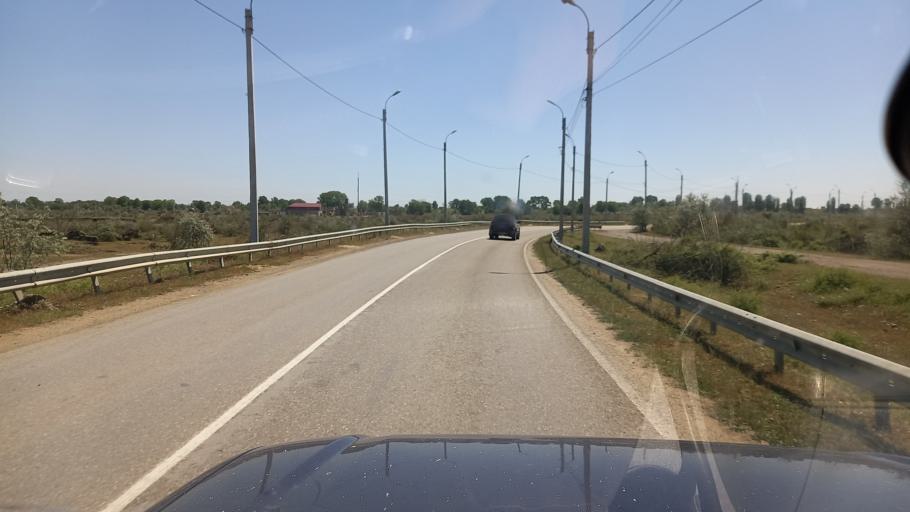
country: RU
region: Dagestan
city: Novaya Maka
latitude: 41.7363
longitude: 48.4504
